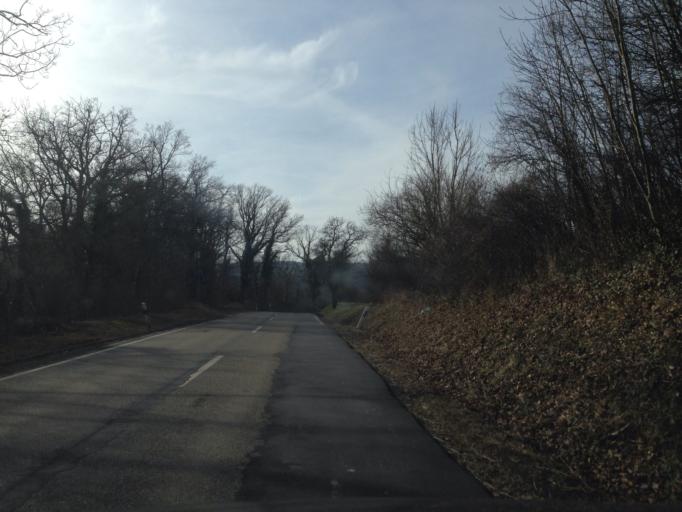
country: DE
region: Baden-Wuerttemberg
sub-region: Regierungsbezirk Stuttgart
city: Widdern
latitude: 49.3095
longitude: 9.4345
